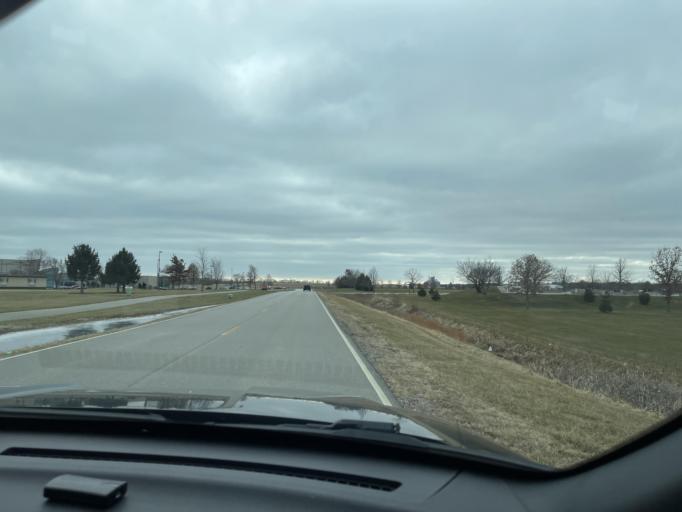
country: US
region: Illinois
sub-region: Sangamon County
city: Jerome
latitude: 39.7599
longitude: -89.7533
